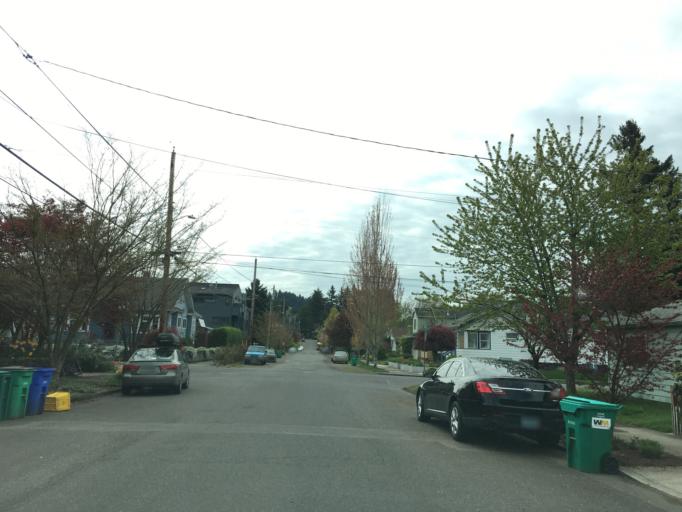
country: US
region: Oregon
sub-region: Multnomah County
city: Lents
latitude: 45.5297
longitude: -122.5986
